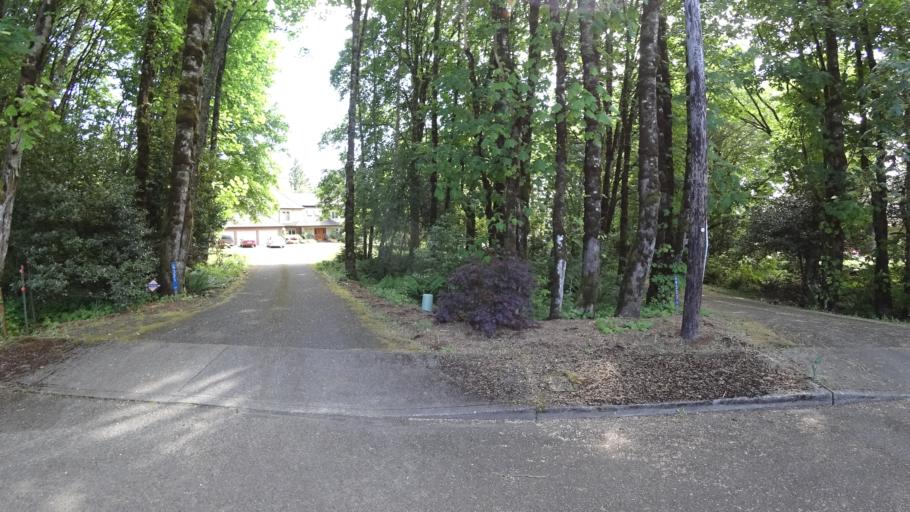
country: US
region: Oregon
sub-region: Washington County
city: Oak Hills
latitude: 45.5893
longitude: -122.8128
